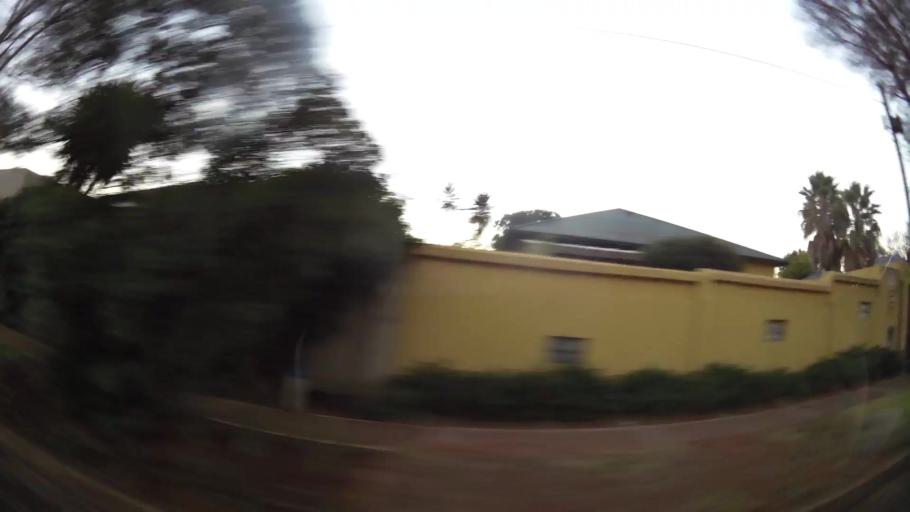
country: ZA
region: Gauteng
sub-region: City of Johannesburg Metropolitan Municipality
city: Roodepoort
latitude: -26.1734
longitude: 27.9184
